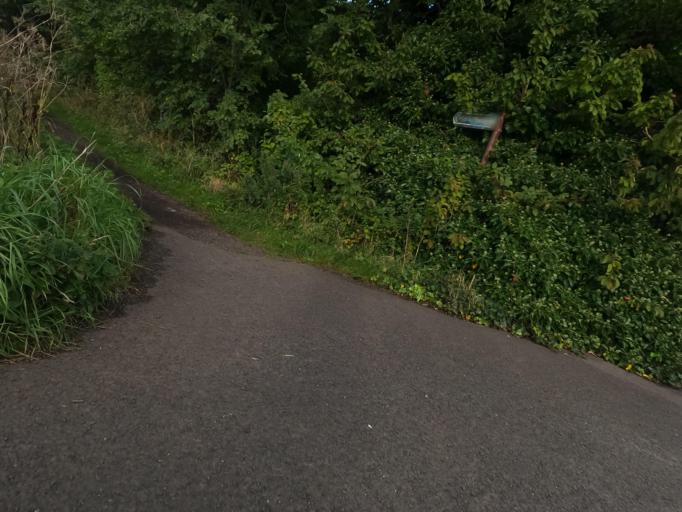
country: GB
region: England
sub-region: Northumberland
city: Seghill
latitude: 55.0689
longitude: -1.5406
